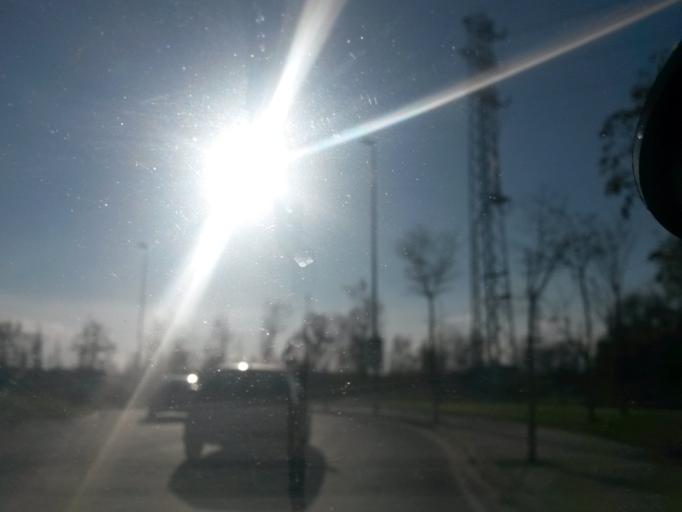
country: ES
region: Catalonia
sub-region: Provincia de Girona
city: Girona
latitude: 41.9851
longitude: 2.8096
